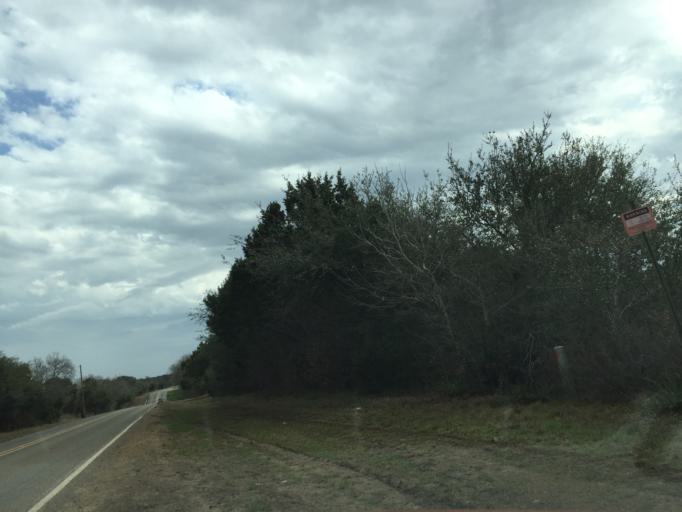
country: US
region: Texas
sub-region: Williamson County
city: Leander
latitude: 30.6603
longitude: -97.9450
